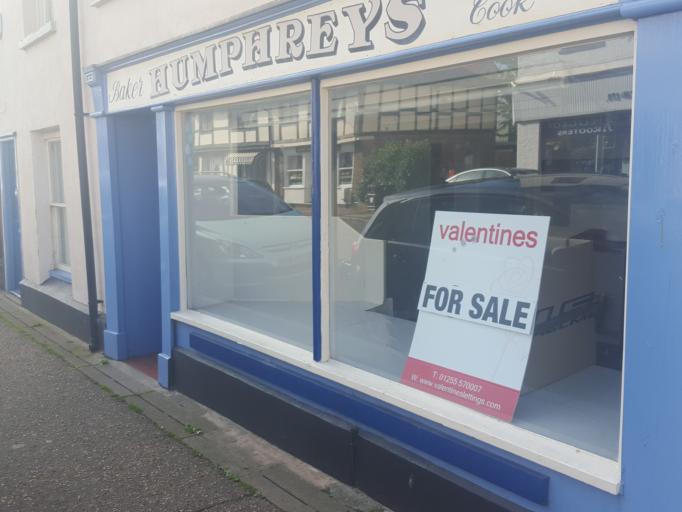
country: GB
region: England
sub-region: Essex
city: Harwich
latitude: 51.9455
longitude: 1.2876
